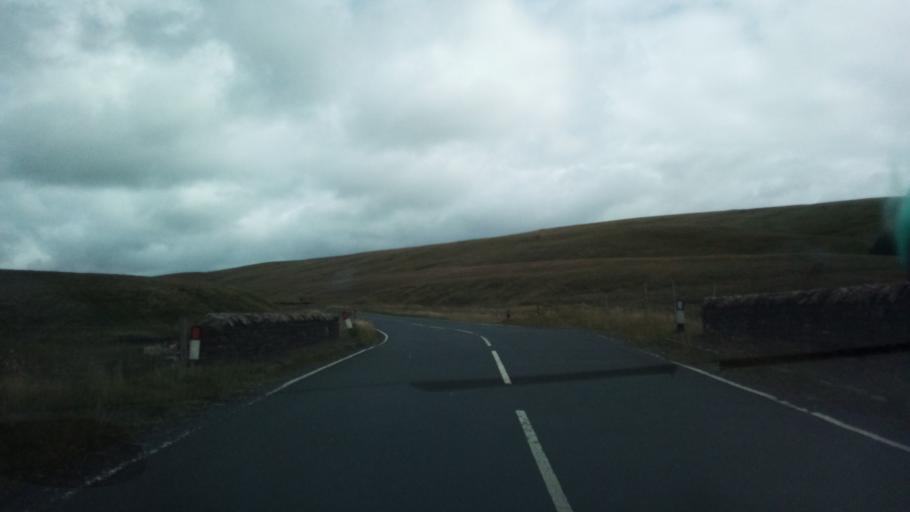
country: GB
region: England
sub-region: North Yorkshire
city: Settle
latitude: 54.2332
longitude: -2.3180
